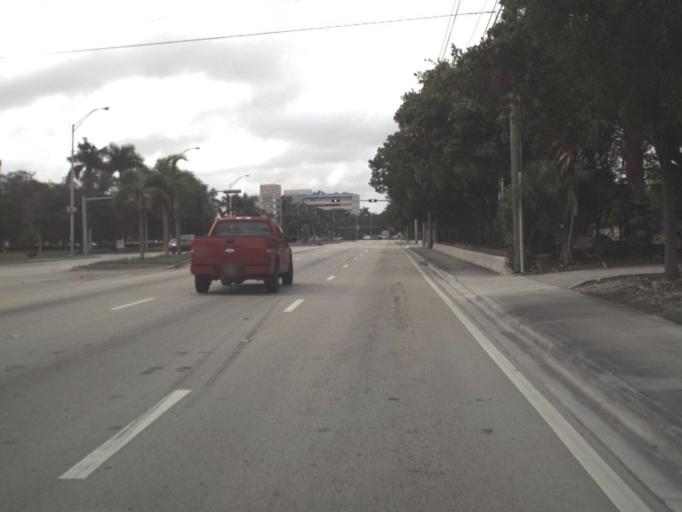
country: US
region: Florida
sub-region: Miami-Dade County
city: Doral
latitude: 25.8100
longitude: -80.3331
